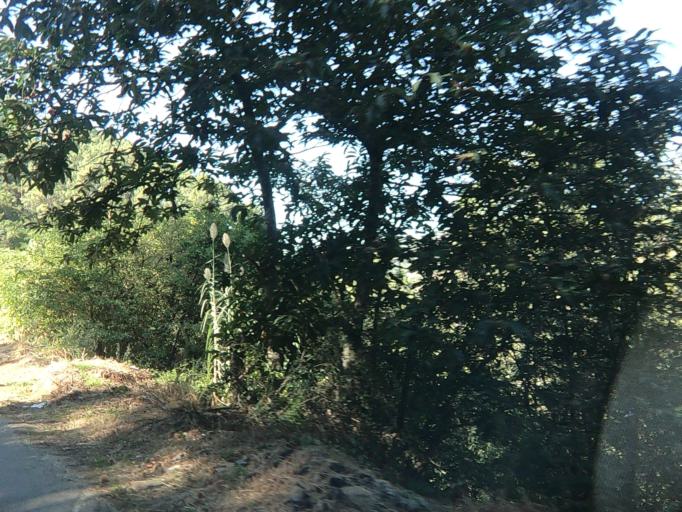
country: PT
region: Vila Real
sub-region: Santa Marta de Penaguiao
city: Santa Marta de Penaguiao
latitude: 41.2380
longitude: -7.8004
